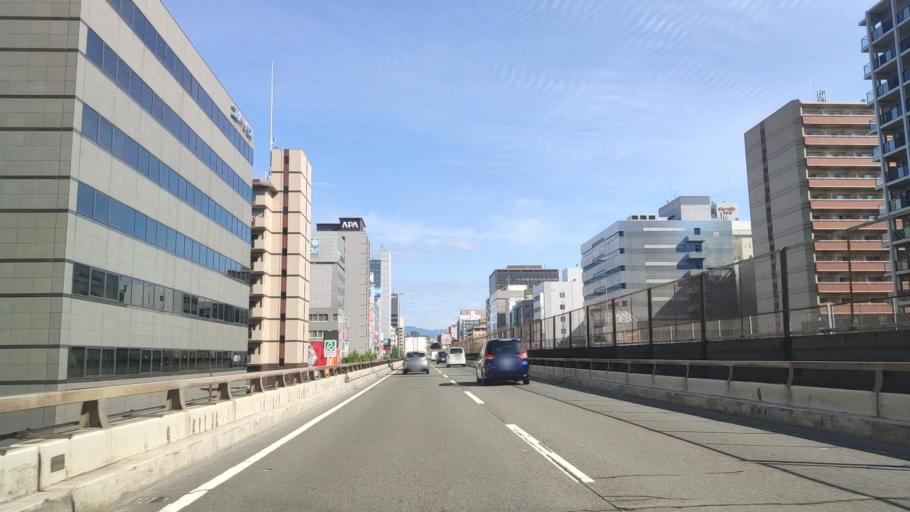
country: JP
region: Osaka
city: Suita
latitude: 34.7553
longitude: 135.4967
